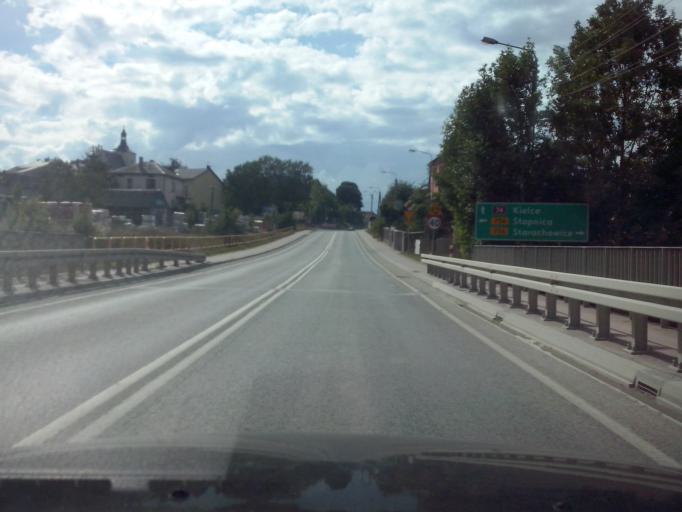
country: PL
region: Swietokrzyskie
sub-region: Powiat kielecki
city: Lagow
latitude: 50.7769
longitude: 21.0876
